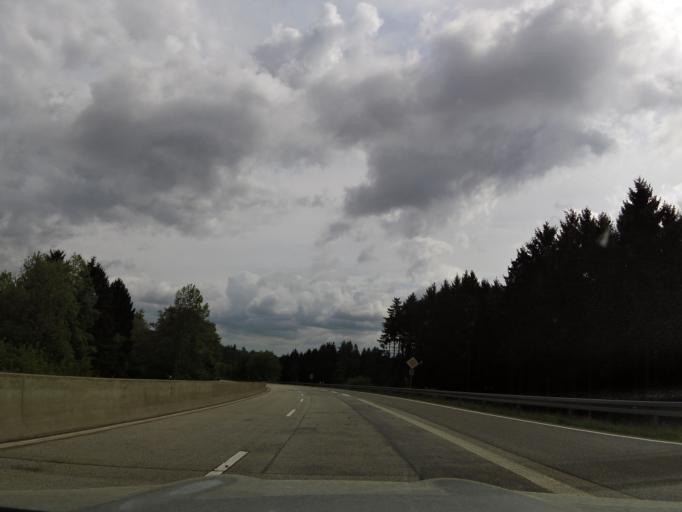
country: DE
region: Hesse
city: Merenberg
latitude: 50.4980
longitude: 8.2241
